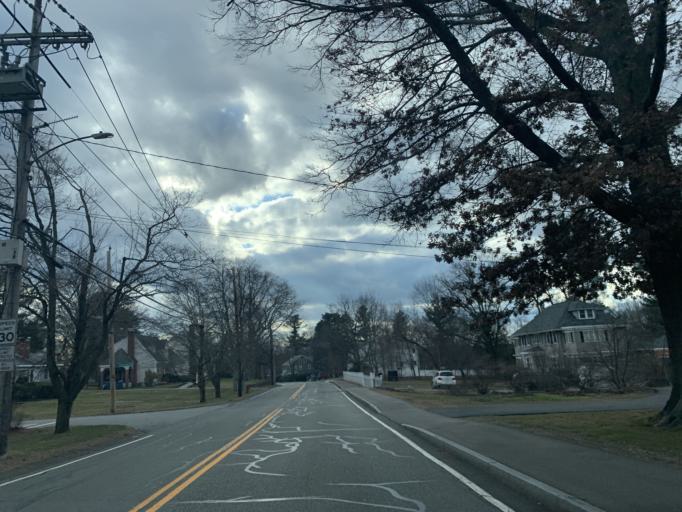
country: US
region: Massachusetts
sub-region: Norfolk County
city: Canton
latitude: 42.1687
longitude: -71.1517
